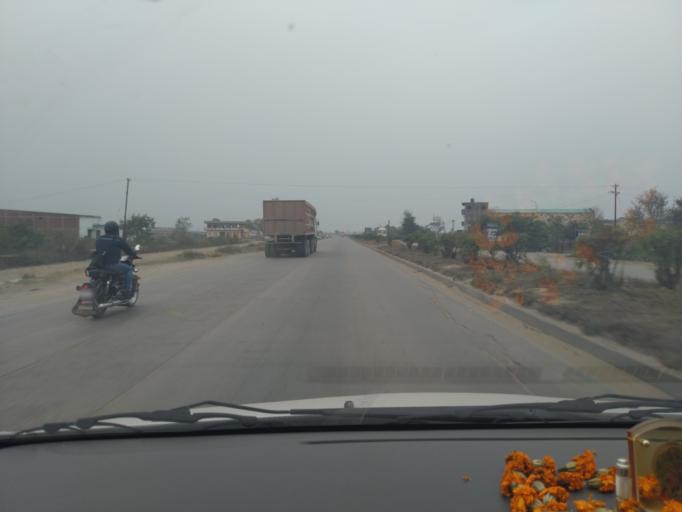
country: IN
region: Bihar
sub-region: Rohtas
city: Dehri
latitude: 24.9657
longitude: 83.9292
